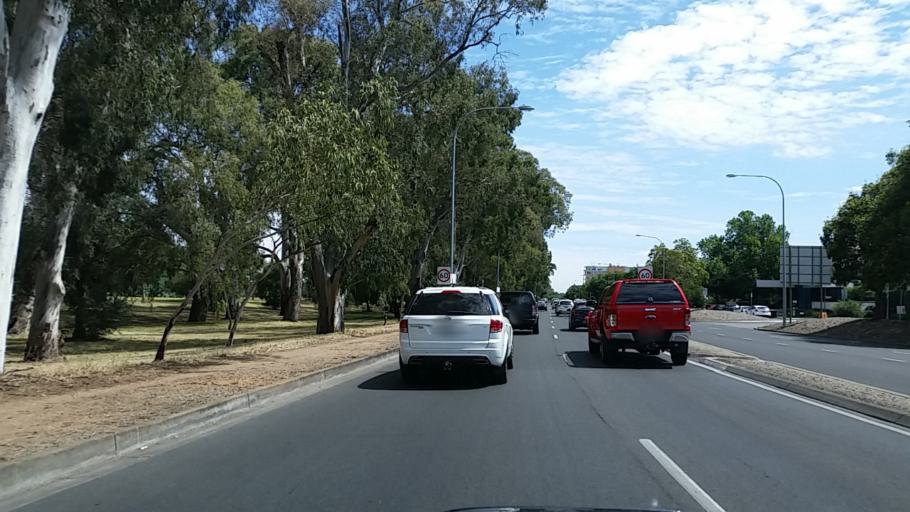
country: AU
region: South Australia
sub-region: Unley
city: Fullarton
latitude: -34.9390
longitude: 138.6242
